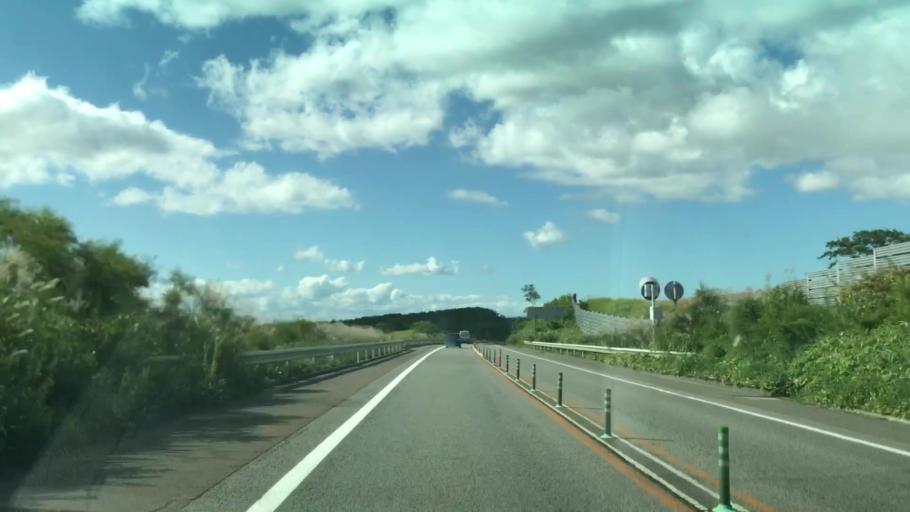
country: JP
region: Hokkaido
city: Muroran
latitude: 42.3982
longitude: 140.9500
